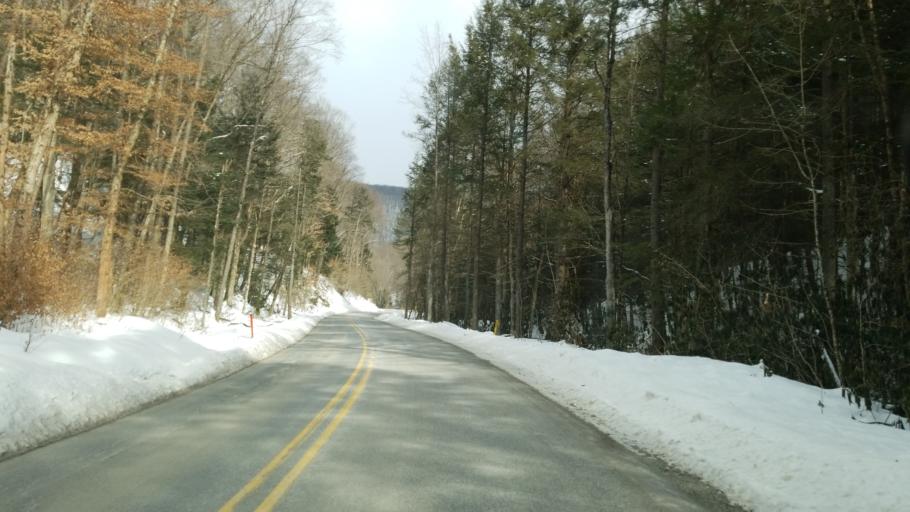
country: US
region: Pennsylvania
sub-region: Clearfield County
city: Shiloh
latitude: 41.2588
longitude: -78.1520
